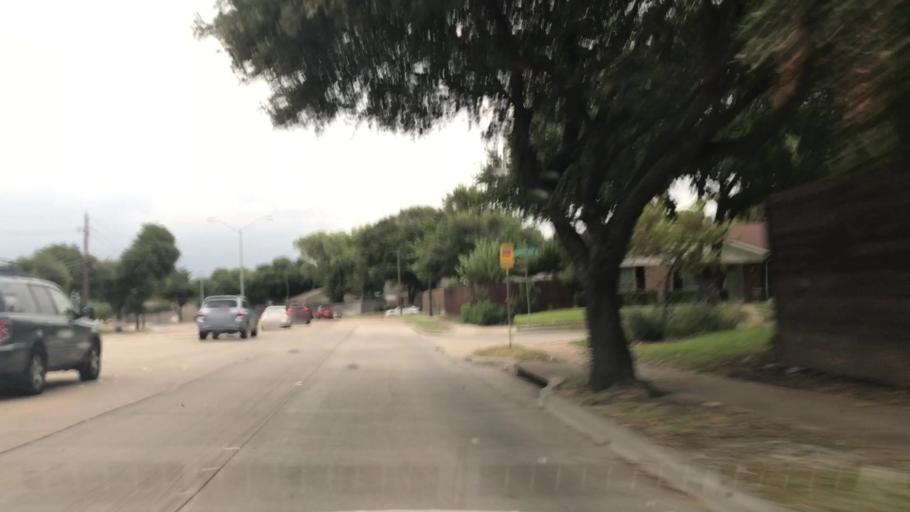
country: US
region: Texas
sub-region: Dallas County
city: Carrollton
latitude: 33.0079
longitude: -96.8871
